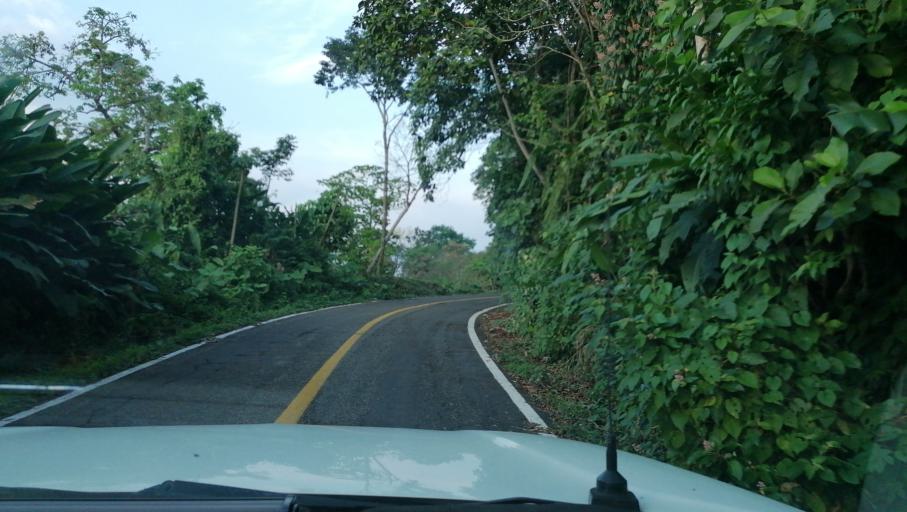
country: MX
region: Chiapas
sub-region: Juarez
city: El Triunfo 1ra. Seccion (Cardona)
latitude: 17.5049
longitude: -93.2349
